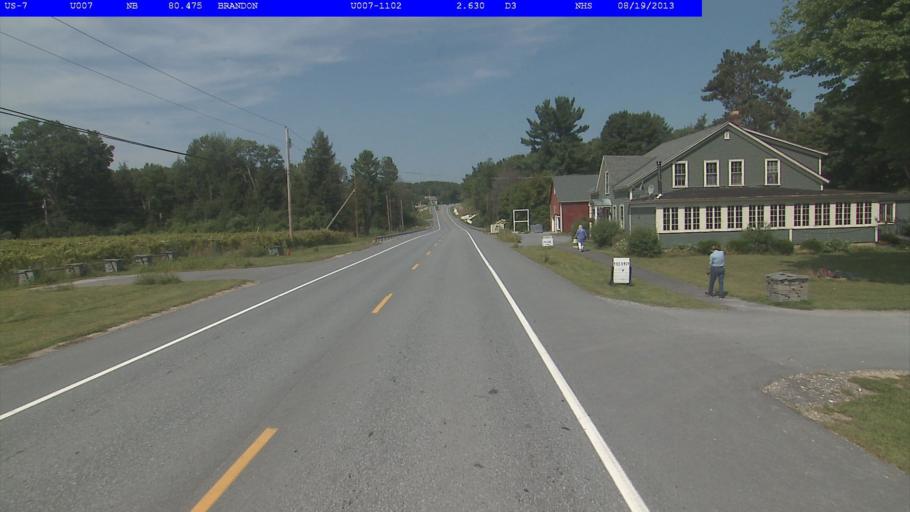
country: US
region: Vermont
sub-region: Rutland County
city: Brandon
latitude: 43.7867
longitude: -73.0695
